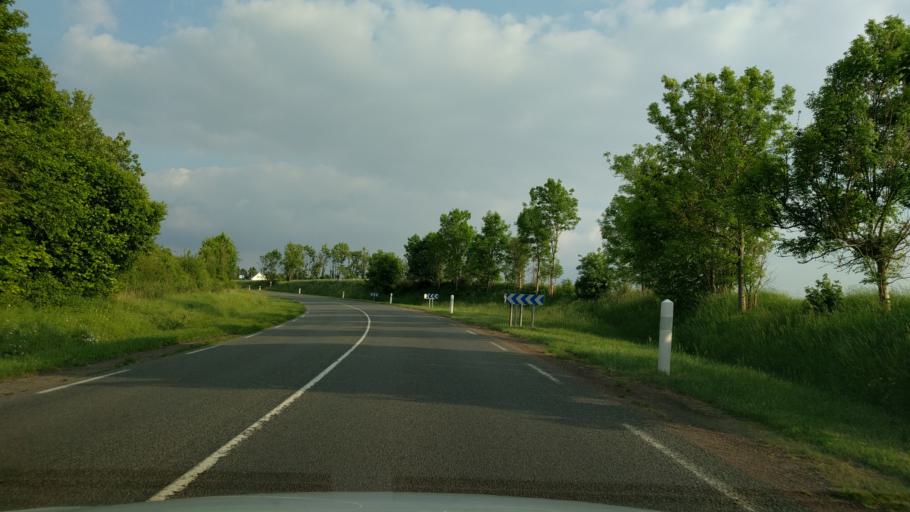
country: FR
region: Picardie
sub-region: Departement de la Somme
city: Peronne
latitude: 49.9513
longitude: 2.9280
